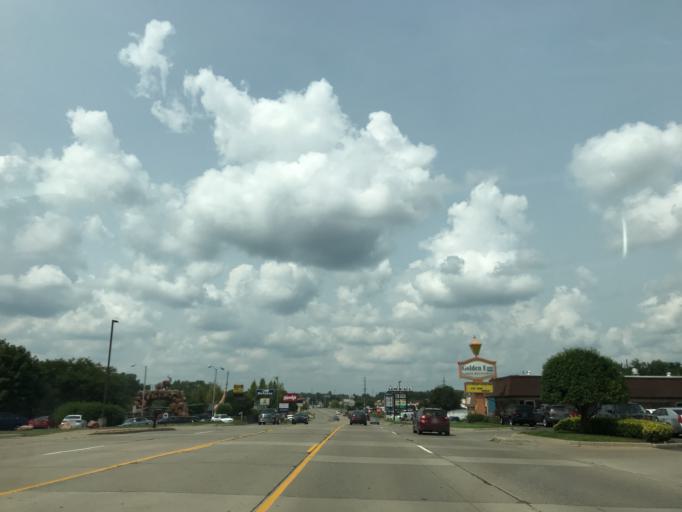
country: US
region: Michigan
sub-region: Washtenaw County
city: Ypsilanti
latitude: 42.2493
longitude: -83.6520
